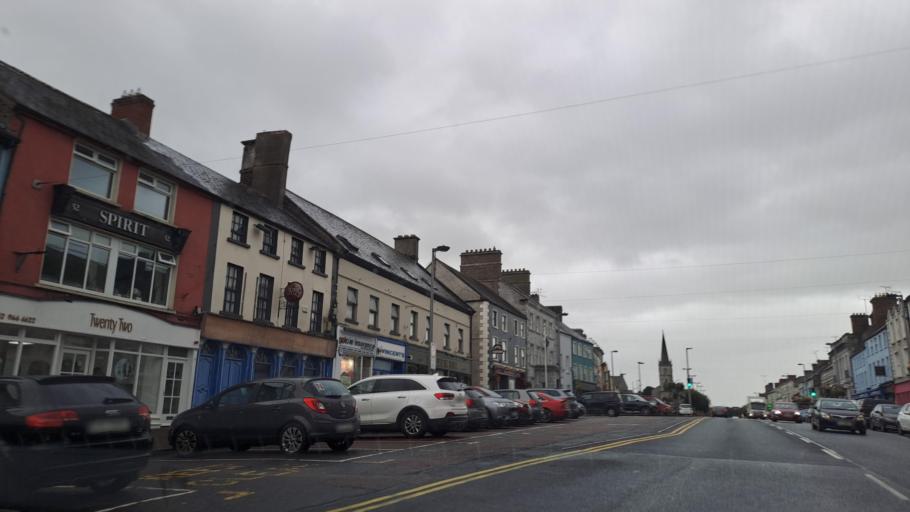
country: IE
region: Ulster
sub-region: County Monaghan
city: Carrickmacross
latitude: 53.9766
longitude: -6.7195
